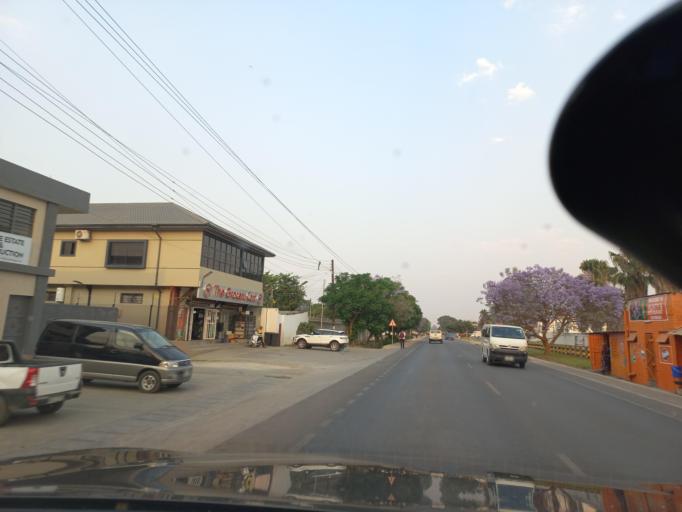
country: ZM
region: Lusaka
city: Lusaka
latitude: -15.3944
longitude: 28.2763
